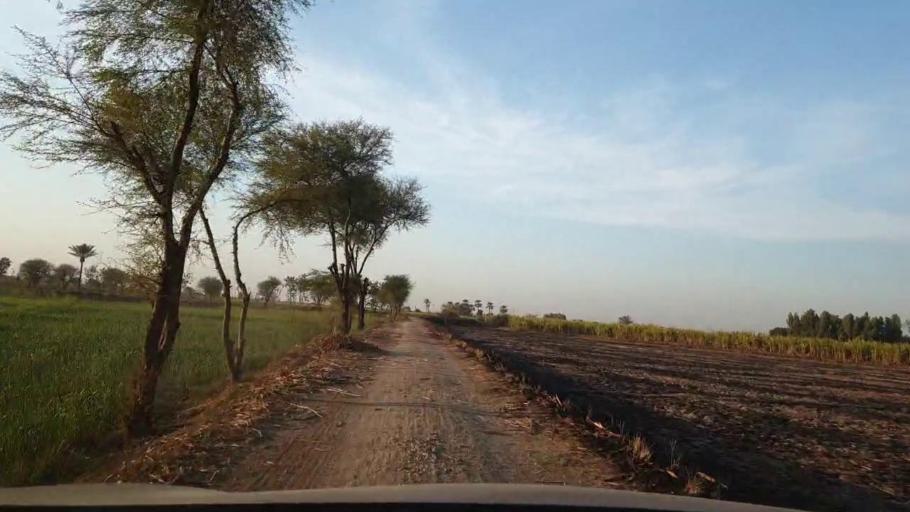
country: PK
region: Sindh
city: Tando Adam
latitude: 25.6139
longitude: 68.6813
